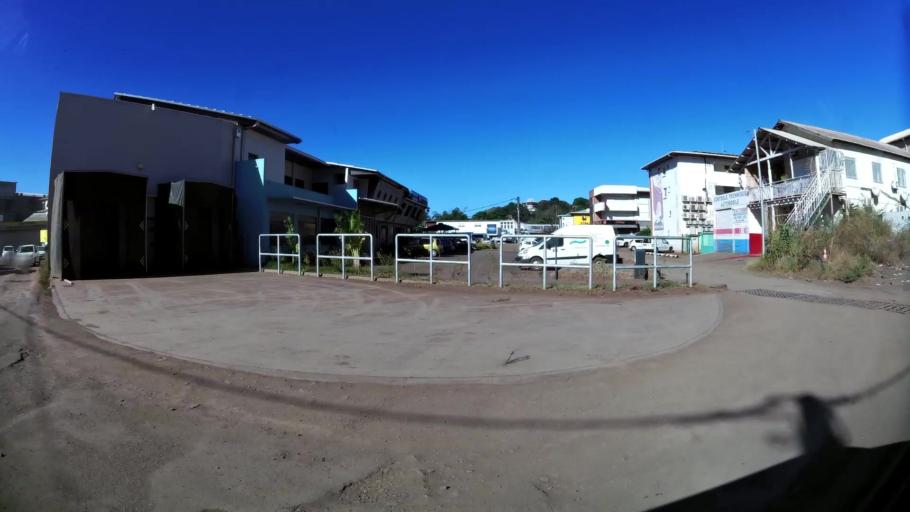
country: YT
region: Mamoudzou
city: Mamoudzou
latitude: -12.7752
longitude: 45.2241
